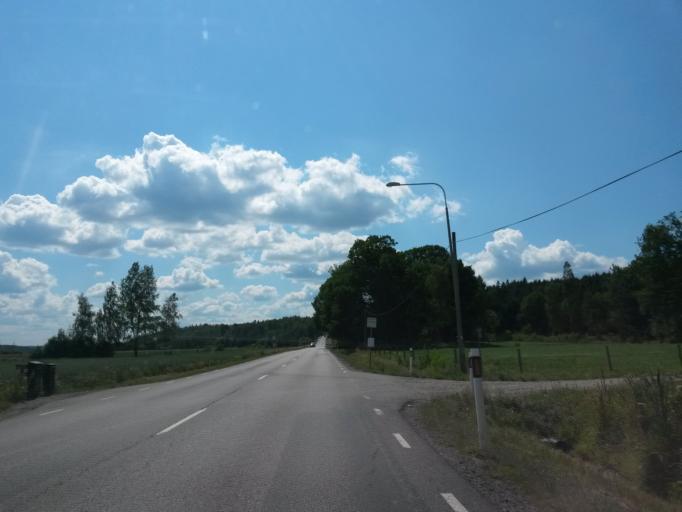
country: SE
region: Vaestra Goetaland
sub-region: Lerums Kommun
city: Grabo
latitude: 57.9074
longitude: 12.3397
